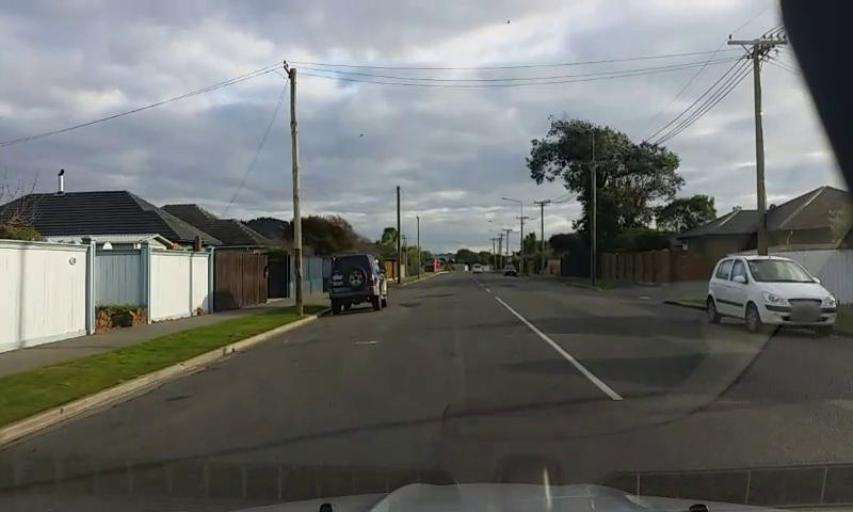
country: NZ
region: Canterbury
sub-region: Christchurch City
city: Christchurch
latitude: -43.5208
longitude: 172.7316
